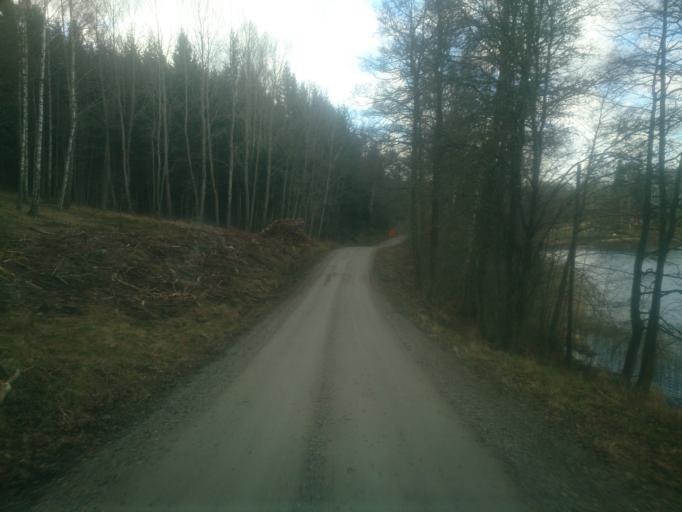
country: SE
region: OEstergoetland
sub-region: Atvidabergs Kommun
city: Atvidaberg
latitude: 58.1961
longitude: 16.1532
